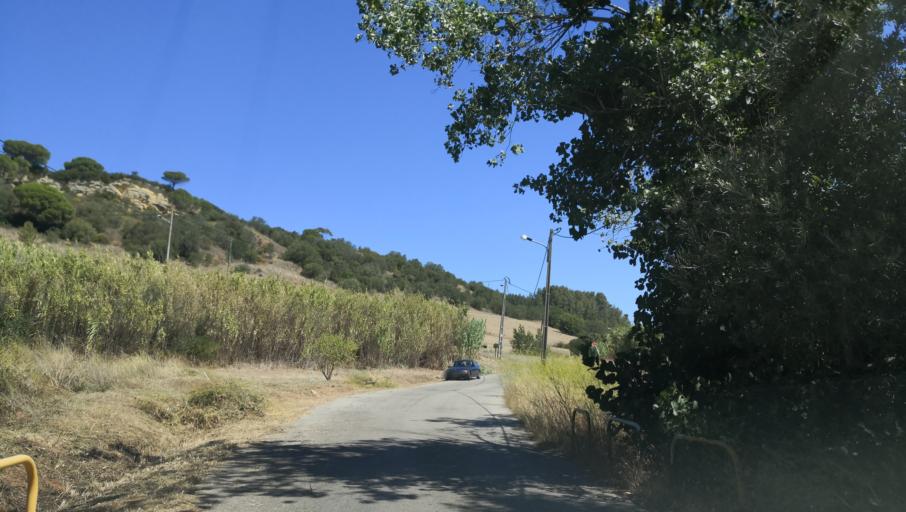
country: PT
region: Setubal
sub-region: Setubal
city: Setubal
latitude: 38.5299
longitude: -8.9206
